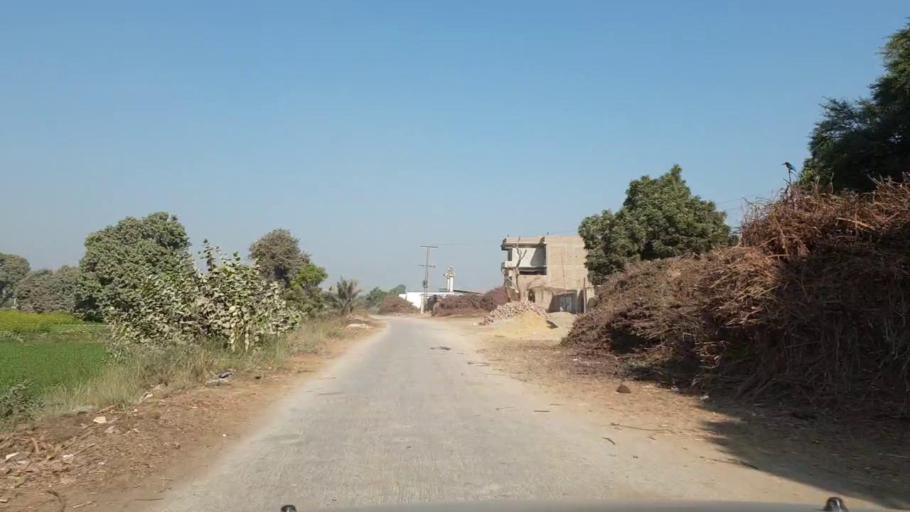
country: PK
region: Sindh
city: Matiari
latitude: 25.5979
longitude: 68.6010
